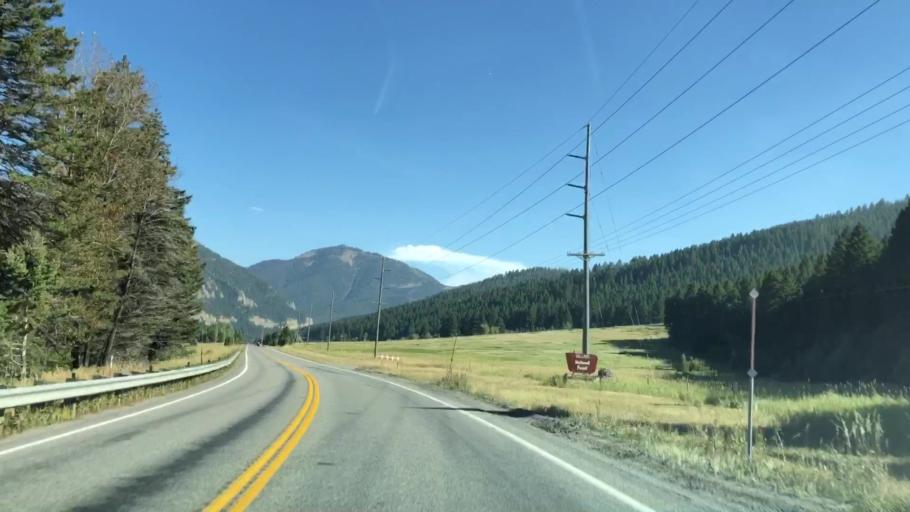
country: US
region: Montana
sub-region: Gallatin County
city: Four Corners
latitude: 45.4716
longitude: -111.2690
